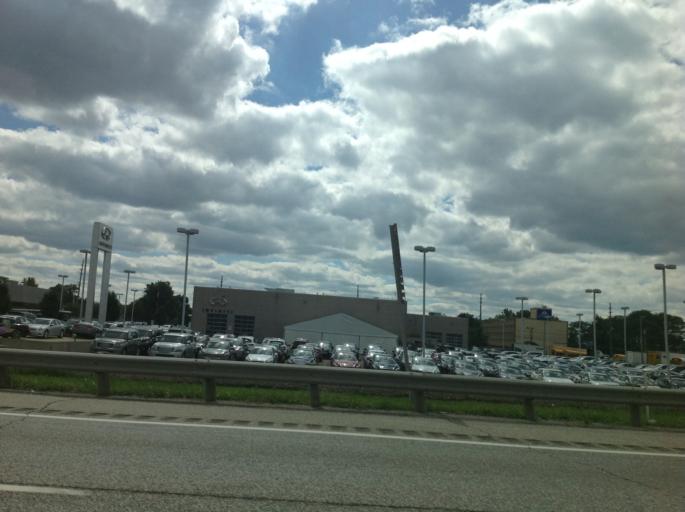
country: US
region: Ohio
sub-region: Cuyahoga County
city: Brook Park
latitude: 41.4203
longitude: -81.7921
